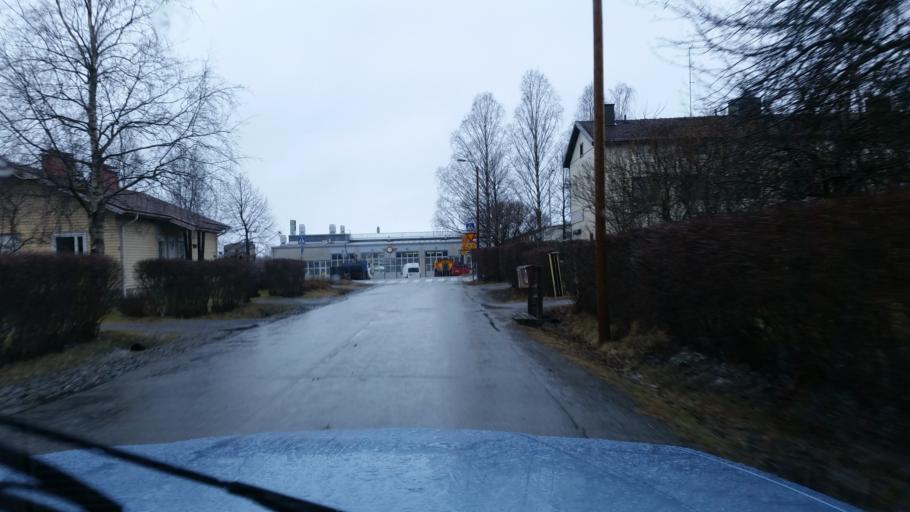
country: FI
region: Pirkanmaa
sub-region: Tampere
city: Tampere
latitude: 61.4785
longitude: 23.7993
